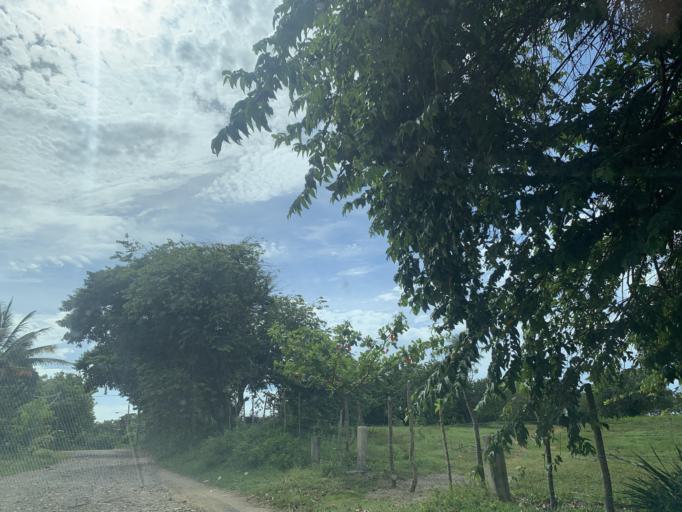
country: DO
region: Puerto Plata
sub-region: Puerto Plata
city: Puerto Plata
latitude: 19.8145
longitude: -70.7190
